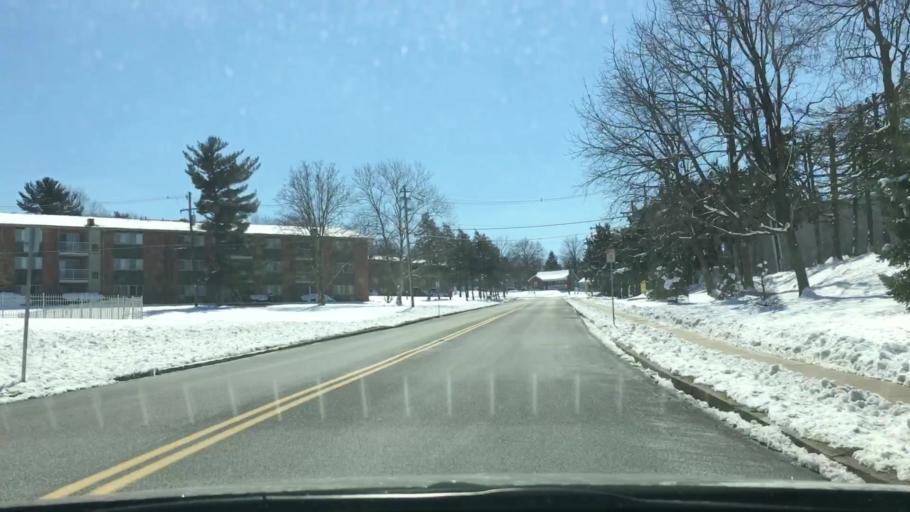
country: US
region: Pennsylvania
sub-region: York County
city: Valley View
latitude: 39.9402
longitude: -76.6906
